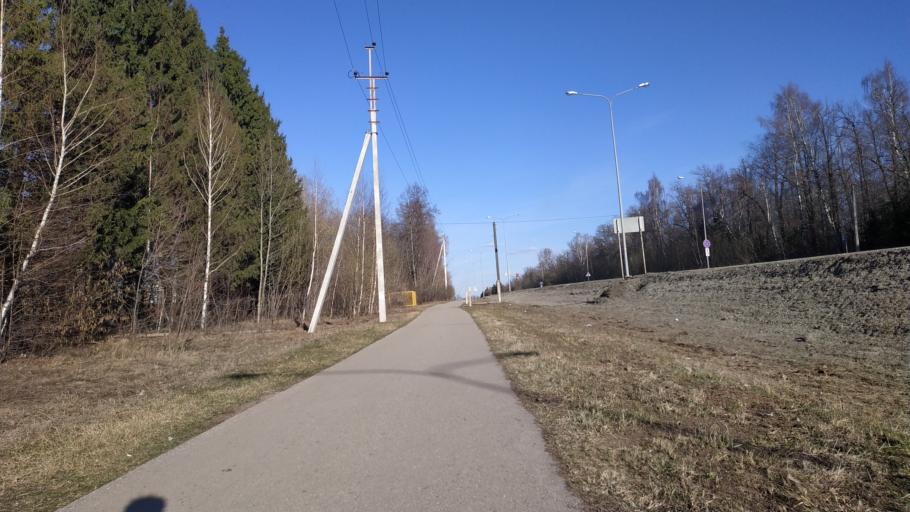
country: RU
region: Chuvashia
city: Novyye Lapsary
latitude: 56.1314
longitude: 47.1460
